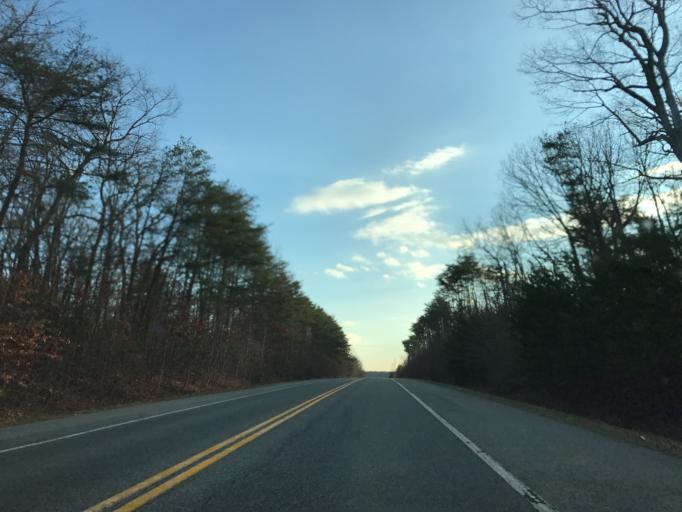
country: US
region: Maryland
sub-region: Cecil County
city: Charlestown
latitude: 39.5689
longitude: -75.9465
